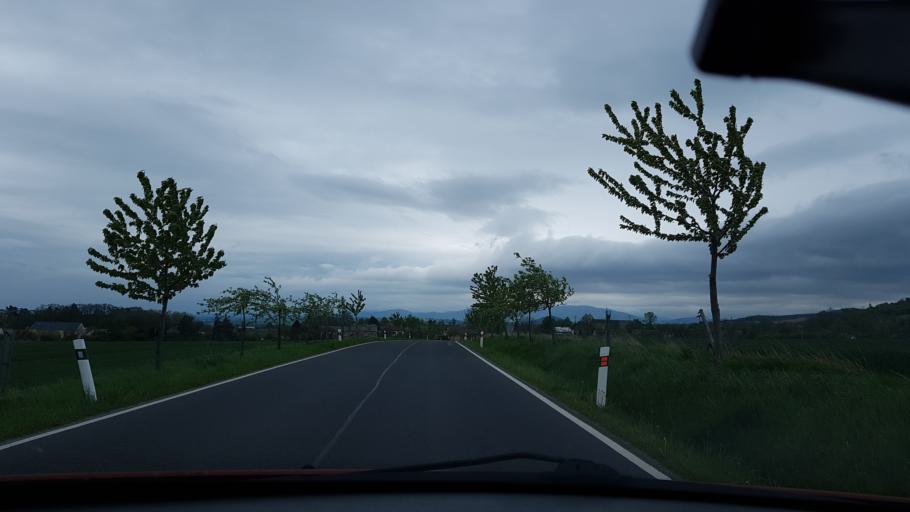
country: CZ
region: Olomoucky
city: Javornik
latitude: 50.4118
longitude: 16.9840
